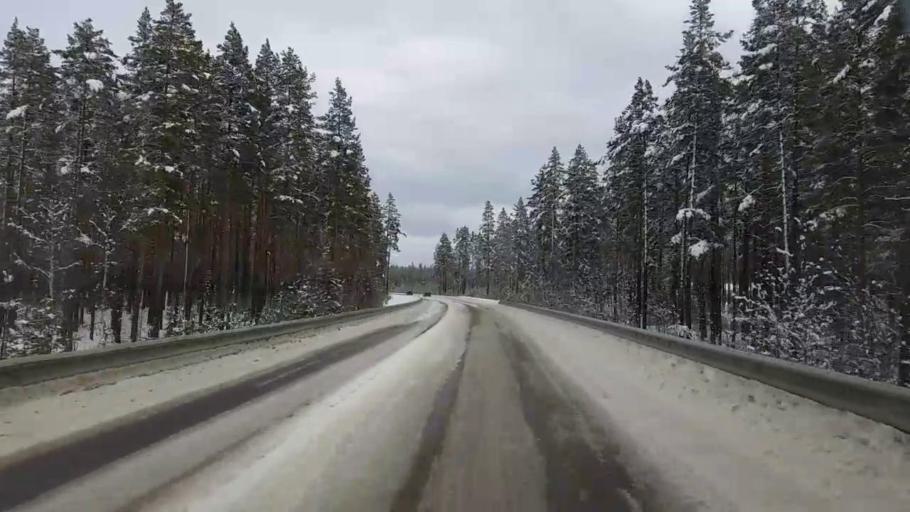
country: SE
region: Vaesternorrland
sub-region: Ange Kommun
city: Ange
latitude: 62.0592
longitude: 15.1180
